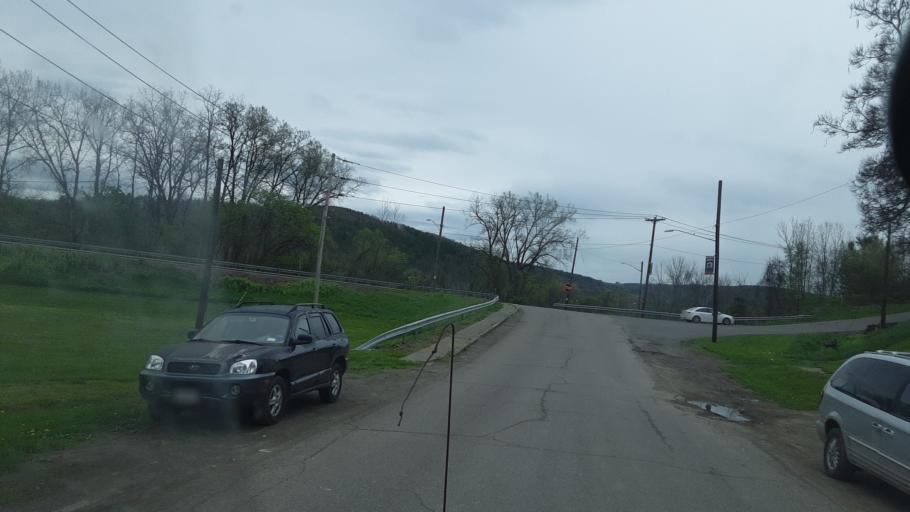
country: US
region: New York
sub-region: Steuben County
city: Addison
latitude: 42.1027
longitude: -77.2428
